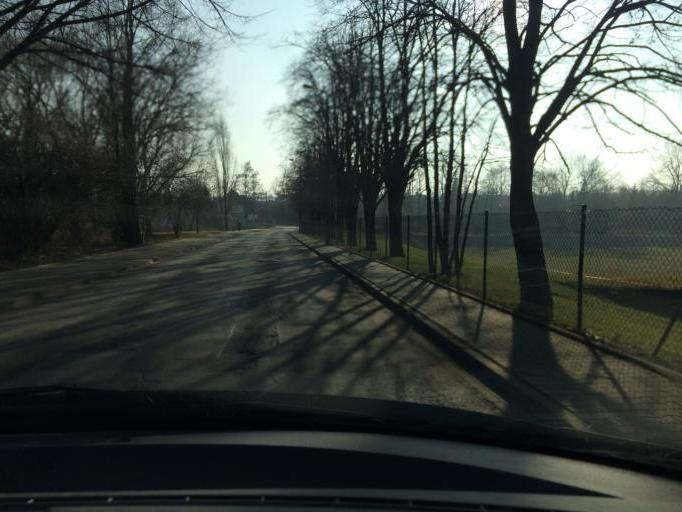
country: PL
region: Lesser Poland Voivodeship
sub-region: Powiat wielicki
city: Czarnochowice
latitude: 50.0113
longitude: 20.0407
